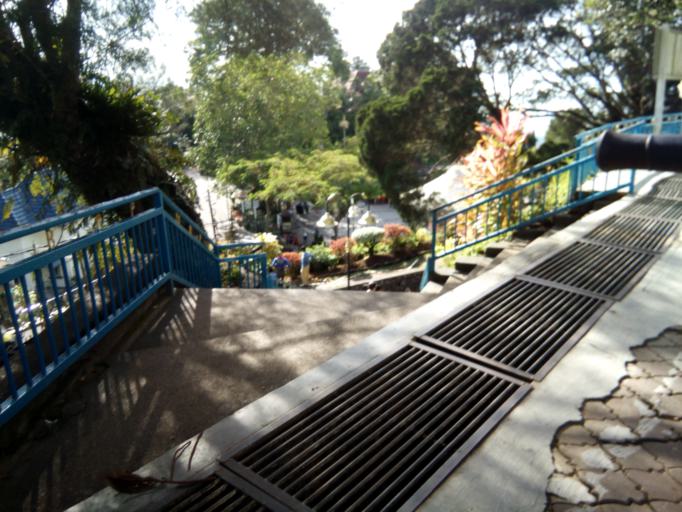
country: MY
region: Penang
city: Tanjung Tokong
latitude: 5.4253
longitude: 100.2686
